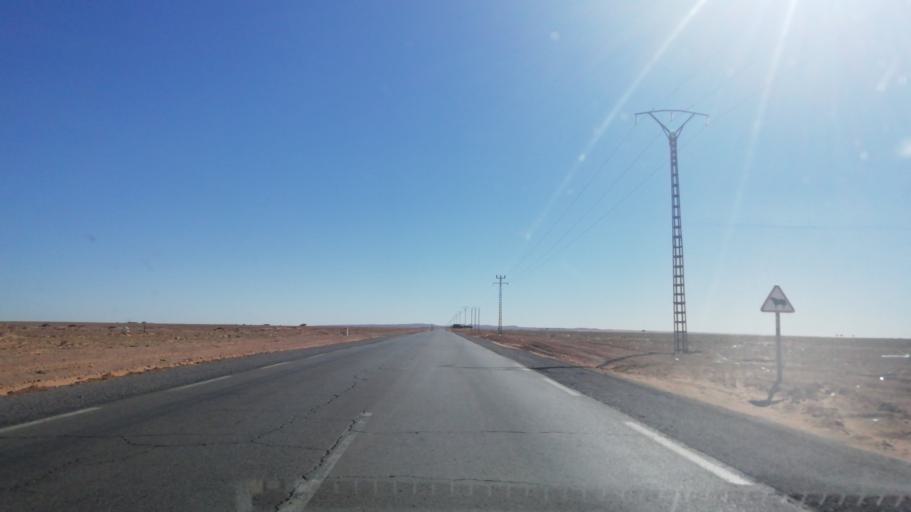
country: DZ
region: Saida
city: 'Ain el Hadjar
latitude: 34.0180
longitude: 0.1078
